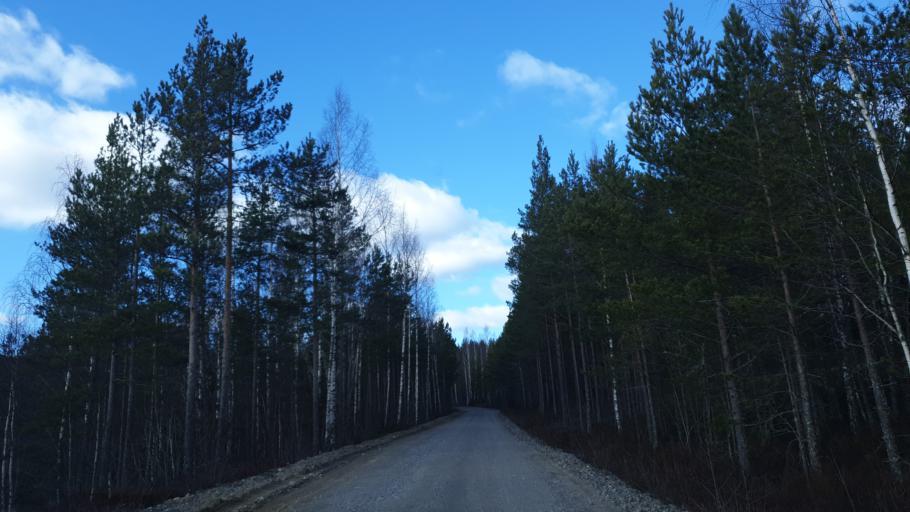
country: SE
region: OErebro
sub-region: Orebro Kommun
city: Garphyttan
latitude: 59.3601
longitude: 14.9787
